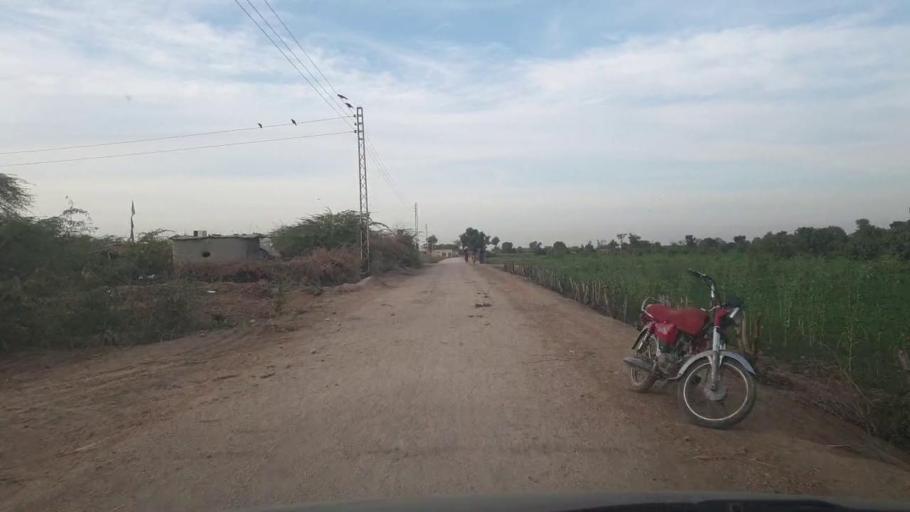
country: PK
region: Sindh
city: Kunri
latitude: 25.2391
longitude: 69.5594
